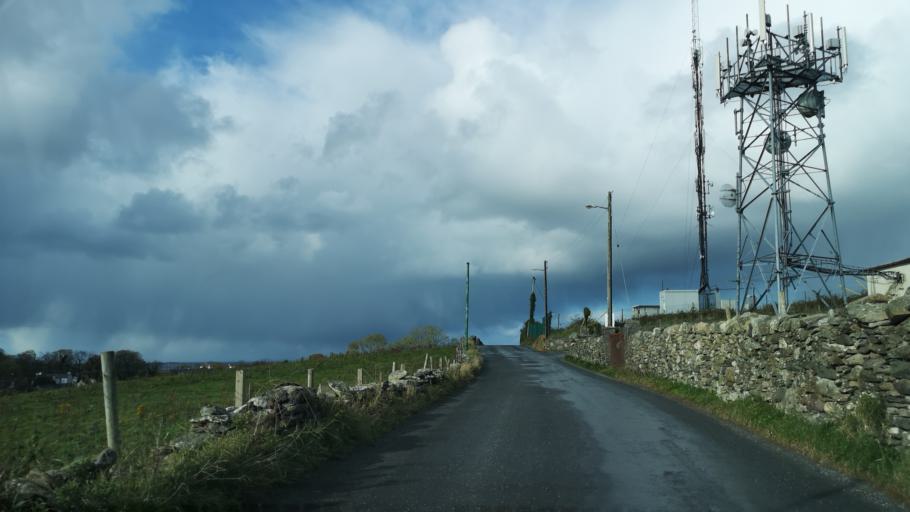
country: IE
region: Connaught
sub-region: Maigh Eo
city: Westport
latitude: 53.7953
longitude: -9.5186
